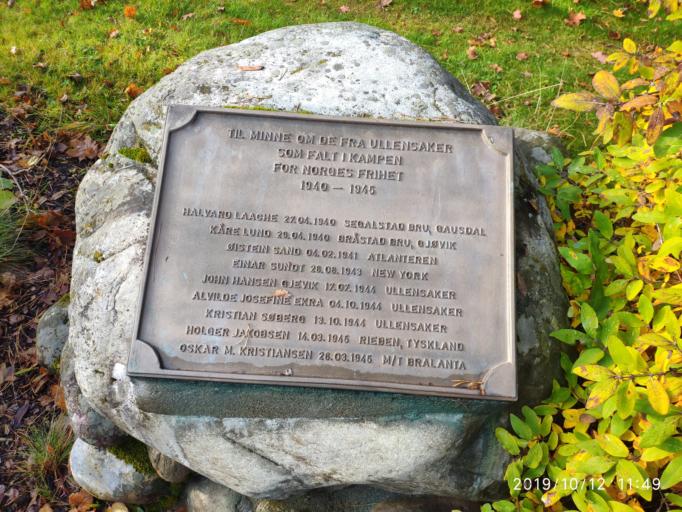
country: NO
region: Akershus
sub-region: Ullensaker
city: Jessheim
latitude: 60.1408
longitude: 11.1742
